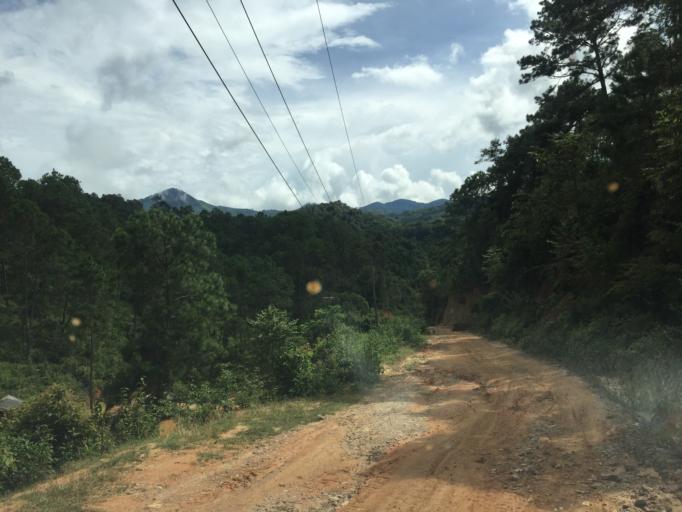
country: LA
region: Xiangkhoang
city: Muang Phonsavan
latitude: 19.3304
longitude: 103.4751
